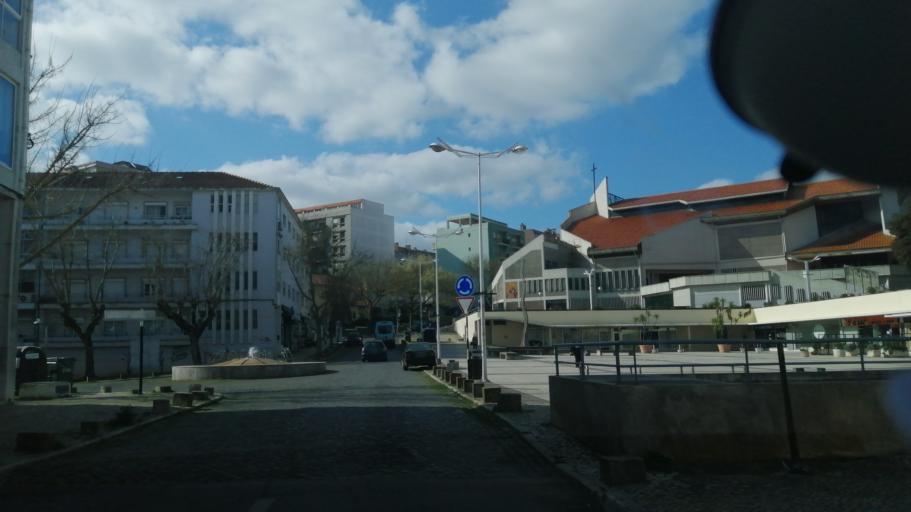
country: PT
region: Setubal
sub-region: Almada
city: Almada
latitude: 38.6811
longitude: -9.1573
